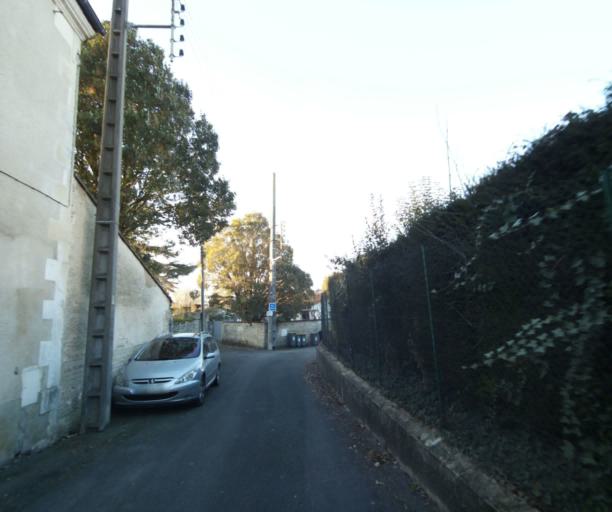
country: FR
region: Poitou-Charentes
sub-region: Departement des Deux-Sevres
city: Niort
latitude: 46.3247
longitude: -0.4740
